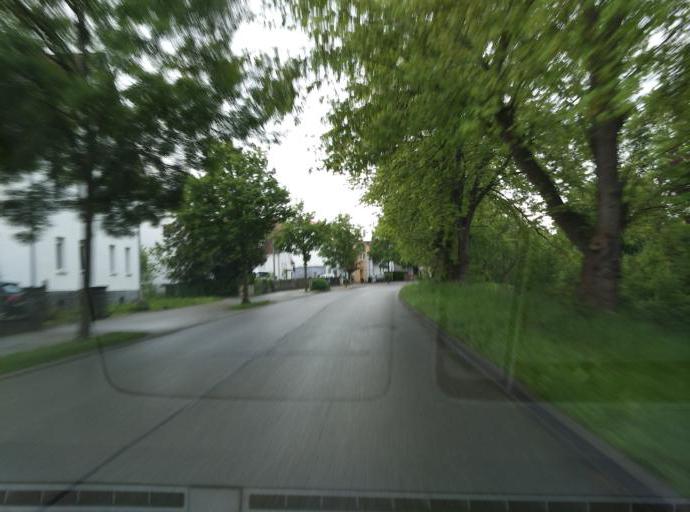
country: DE
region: Baden-Wuerttemberg
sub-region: Tuebingen Region
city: Wannweil
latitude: 48.5190
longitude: 9.1482
